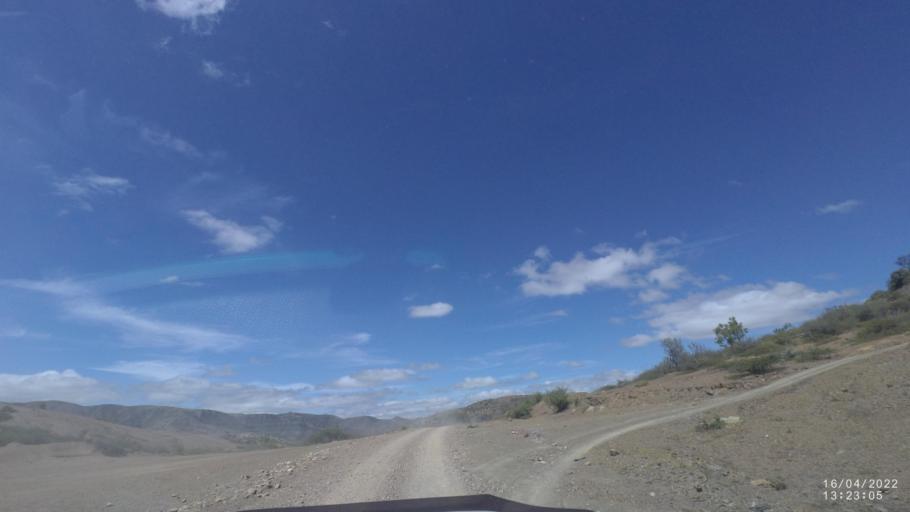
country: BO
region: Cochabamba
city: Mizque
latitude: -17.9938
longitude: -65.6026
